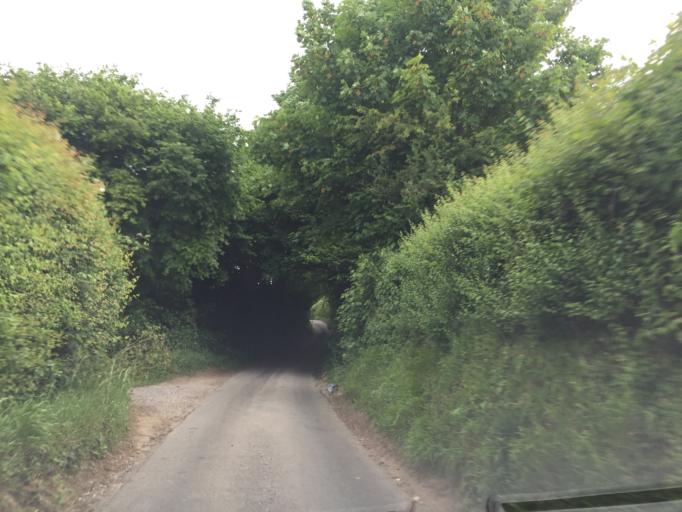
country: GB
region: England
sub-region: Dorset
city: Bovington Camp
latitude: 50.7295
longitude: -2.3305
